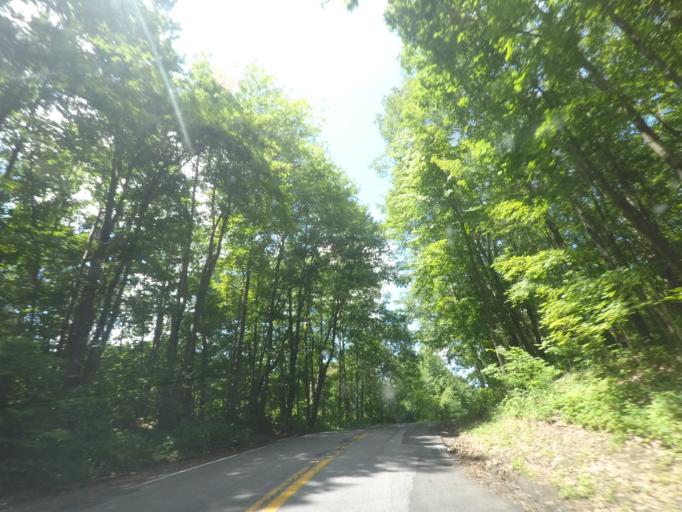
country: US
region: New York
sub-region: Albany County
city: Voorheesville
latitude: 42.7136
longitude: -73.9591
